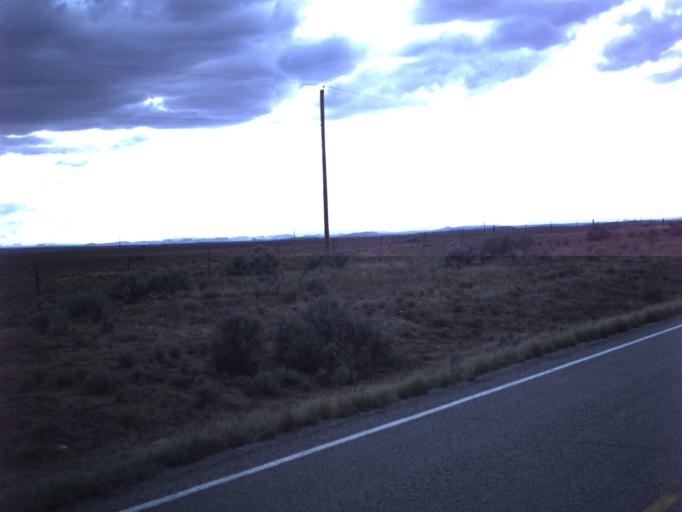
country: US
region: Utah
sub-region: San Juan County
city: Blanding
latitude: 37.4310
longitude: -109.3641
